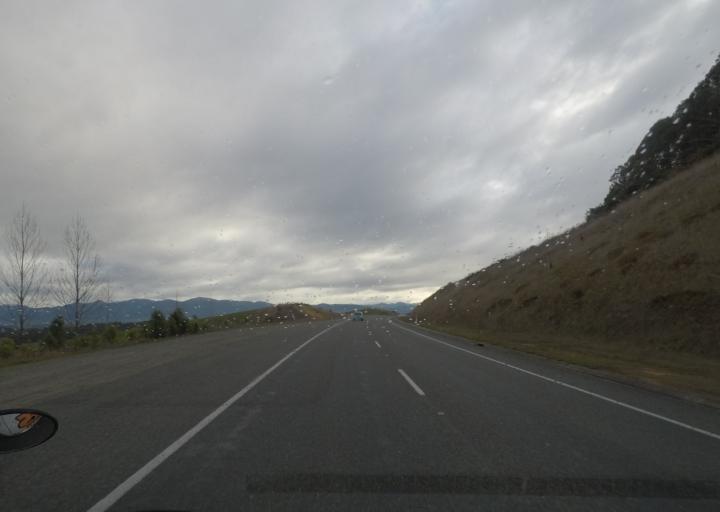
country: NZ
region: Tasman
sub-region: Tasman District
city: Mapua
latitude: -41.2374
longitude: 173.0517
